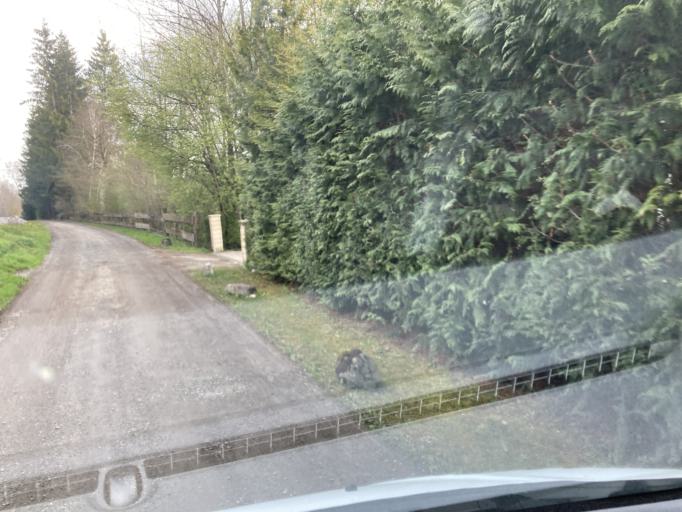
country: DE
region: Bavaria
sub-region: Upper Bavaria
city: Grafing bei Munchen
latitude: 48.0426
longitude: 11.9545
